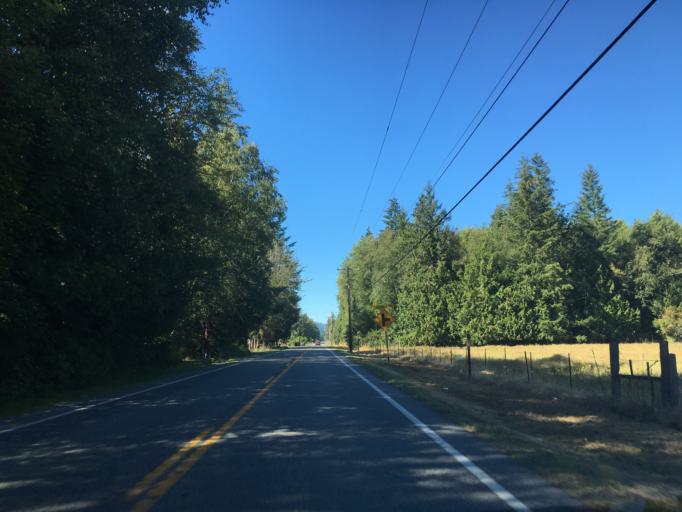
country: US
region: Washington
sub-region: Skagit County
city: Sedro-Woolley
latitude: 48.5629
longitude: -122.2247
